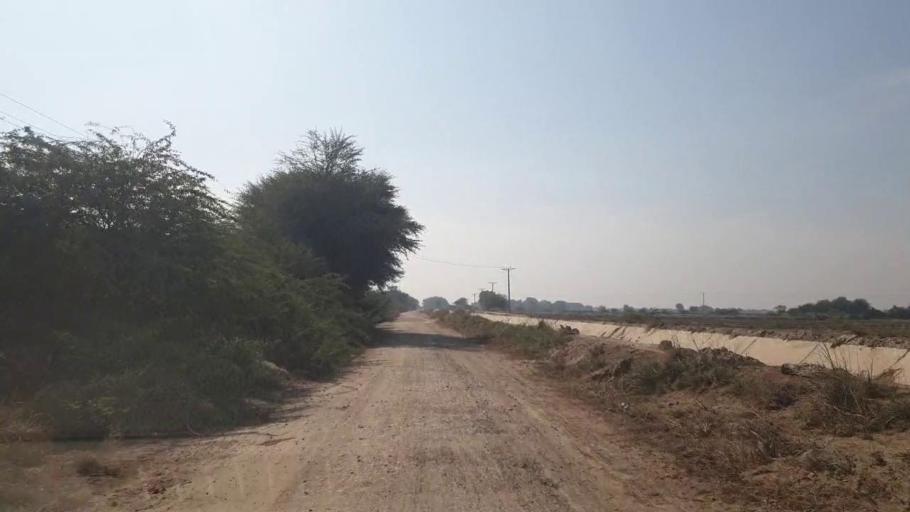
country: PK
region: Sindh
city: Matiari
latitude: 25.6649
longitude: 68.3453
